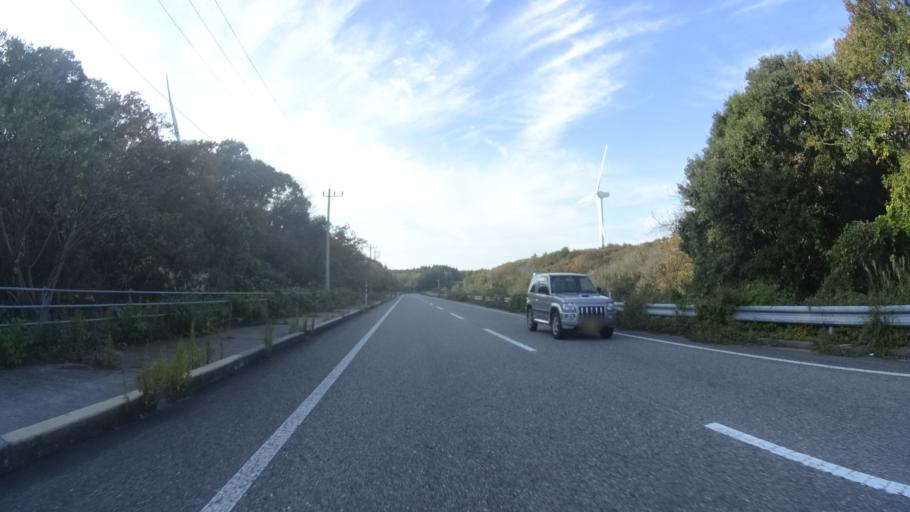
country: JP
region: Ishikawa
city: Hakui
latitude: 37.0728
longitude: 136.7337
